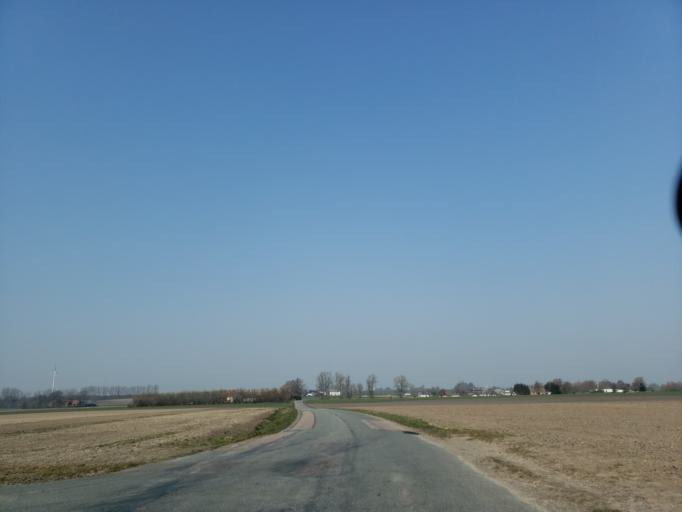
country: SE
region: Skane
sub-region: Simrishamns Kommun
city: Simrishamn
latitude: 55.4615
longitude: 14.2110
